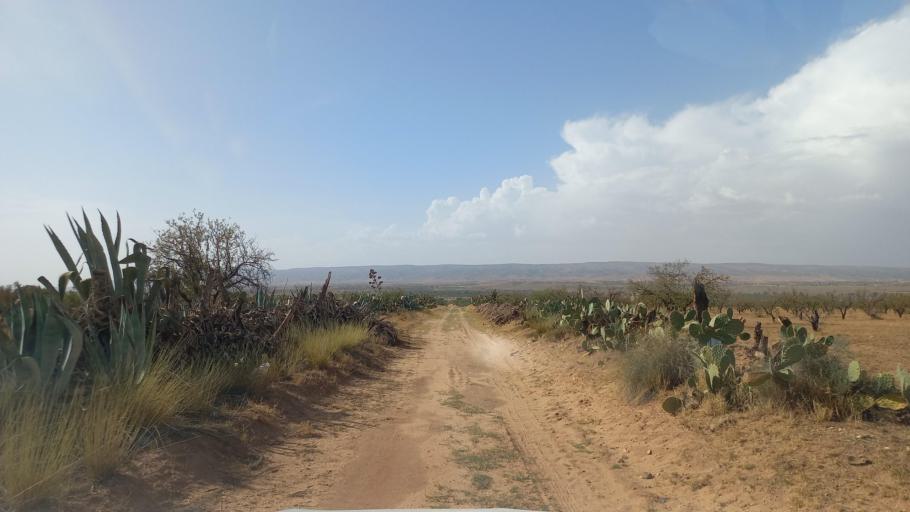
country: TN
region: Al Qasrayn
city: Kasserine
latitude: 35.2058
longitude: 8.9600
